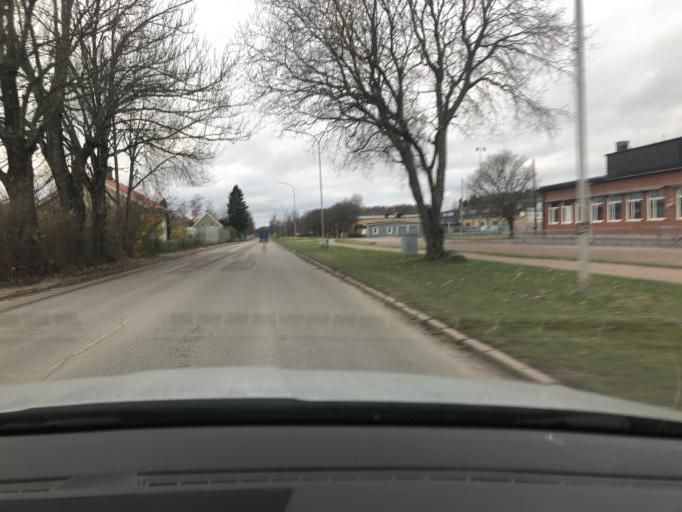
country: SE
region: Uppsala
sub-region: Tierps Kommun
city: Tierp
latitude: 60.3453
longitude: 17.5048
